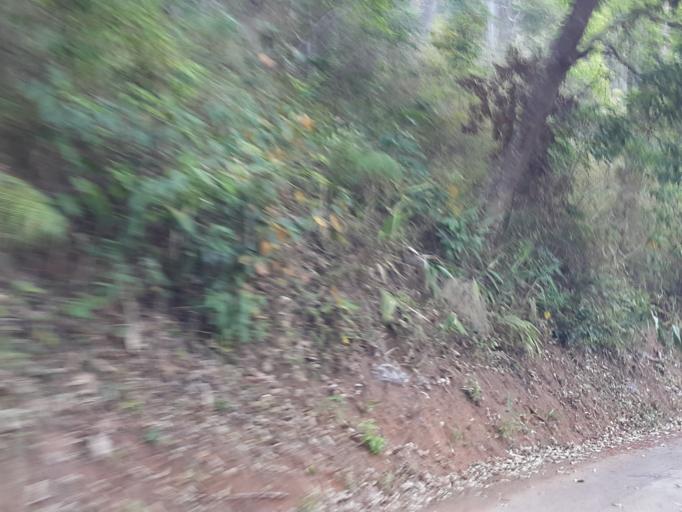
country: TH
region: Chiang Mai
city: Samoeng
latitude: 18.9114
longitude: 98.7975
